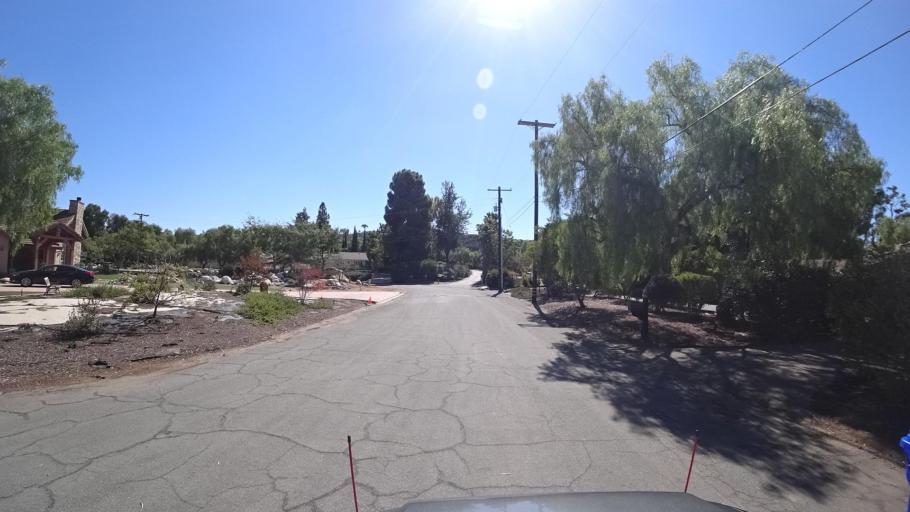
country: US
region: California
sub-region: San Diego County
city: Bonita
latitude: 32.6579
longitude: -117.0365
